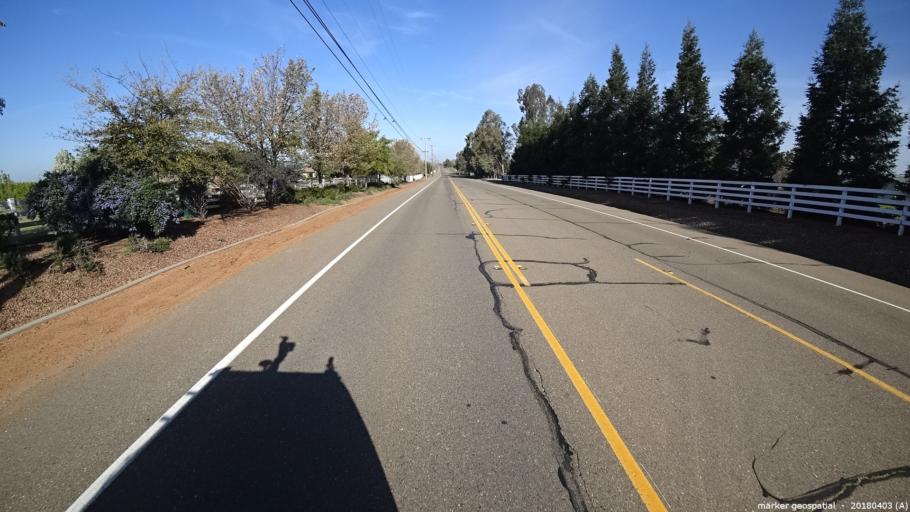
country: US
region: California
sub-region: Sacramento County
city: Clay
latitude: 38.4162
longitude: -121.1803
